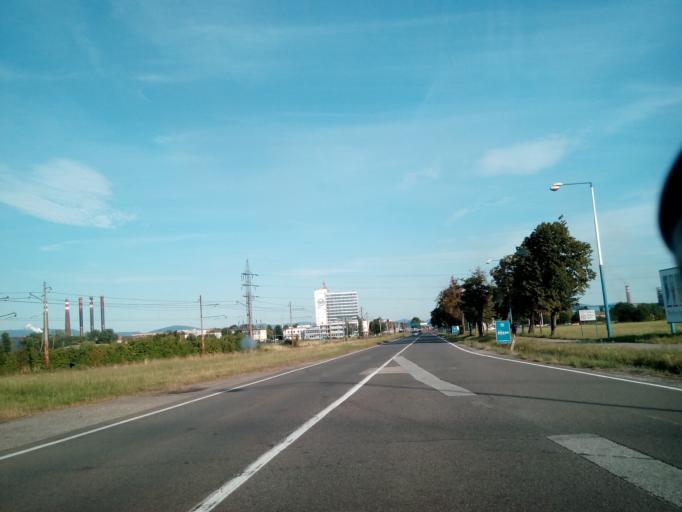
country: SK
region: Kosicky
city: Kosice
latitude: 48.6273
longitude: 21.1854
